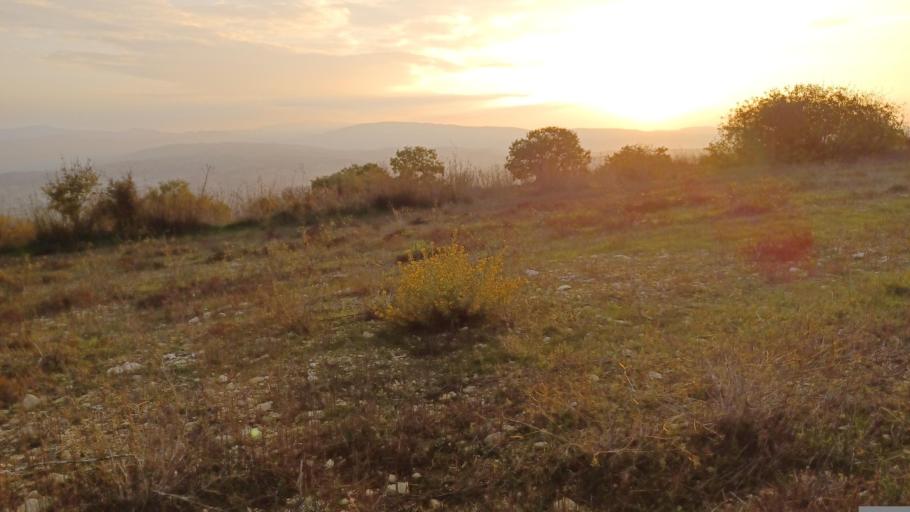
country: CY
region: Pafos
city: Pegeia
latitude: 34.9107
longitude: 32.4426
